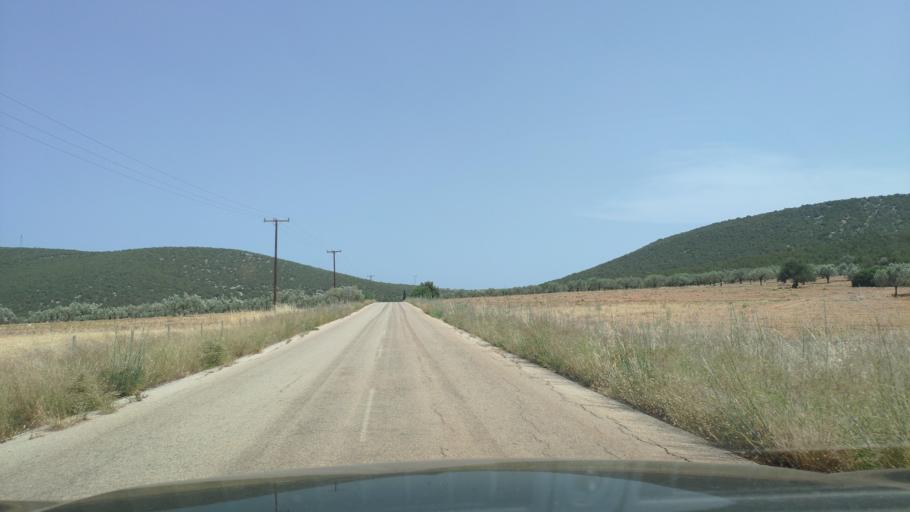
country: GR
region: Peloponnese
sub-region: Nomos Argolidos
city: Didyma
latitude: 37.4520
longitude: 23.1752
